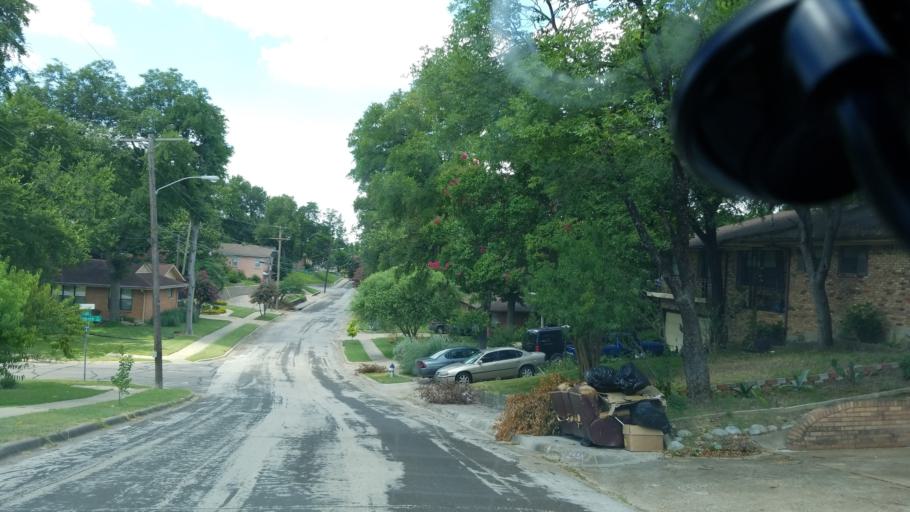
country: US
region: Texas
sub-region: Dallas County
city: Cockrell Hill
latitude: 32.7007
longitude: -96.8598
